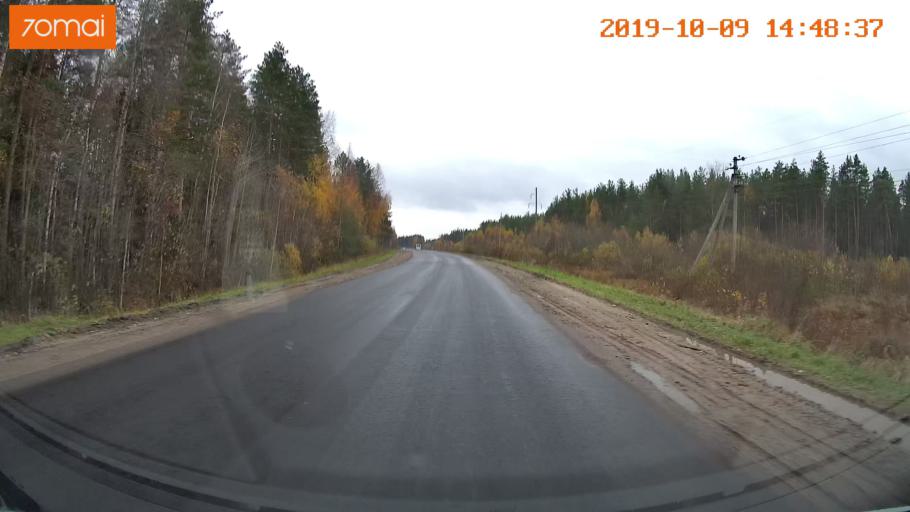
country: RU
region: Kostroma
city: Chistyye Bory
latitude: 58.4031
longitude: 41.5762
